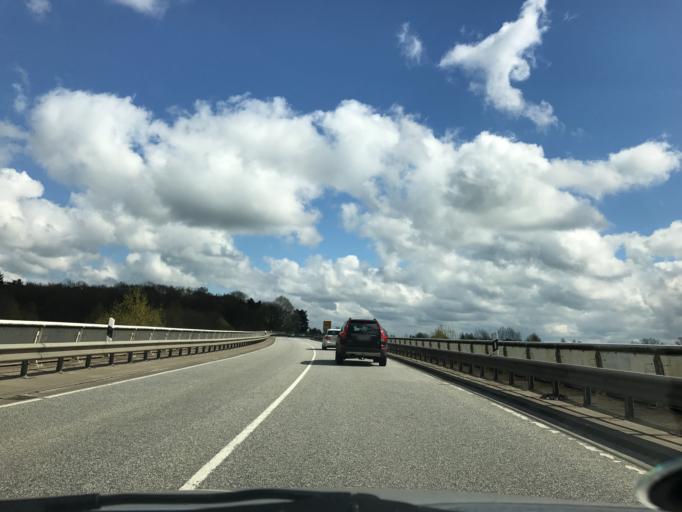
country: DE
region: Schleswig-Holstein
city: Preetz
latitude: 54.2479
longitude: 10.2848
